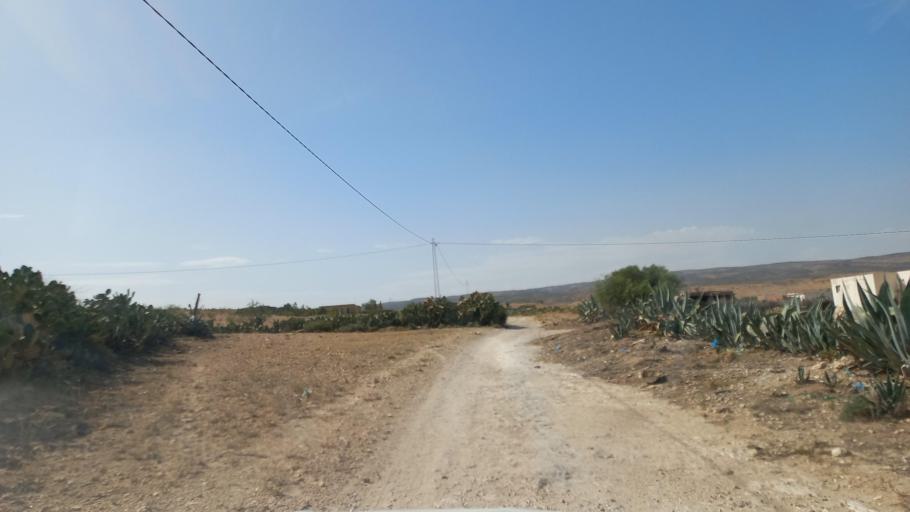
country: TN
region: Al Qasrayn
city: Kasserine
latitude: 35.2771
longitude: 8.9417
